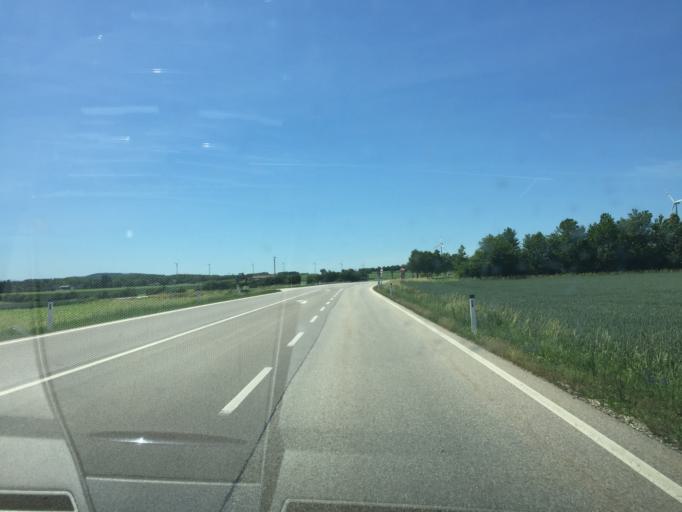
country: AT
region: Lower Austria
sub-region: Politischer Bezirk Sankt Polten
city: Kapelln
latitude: 48.2554
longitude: 15.7476
